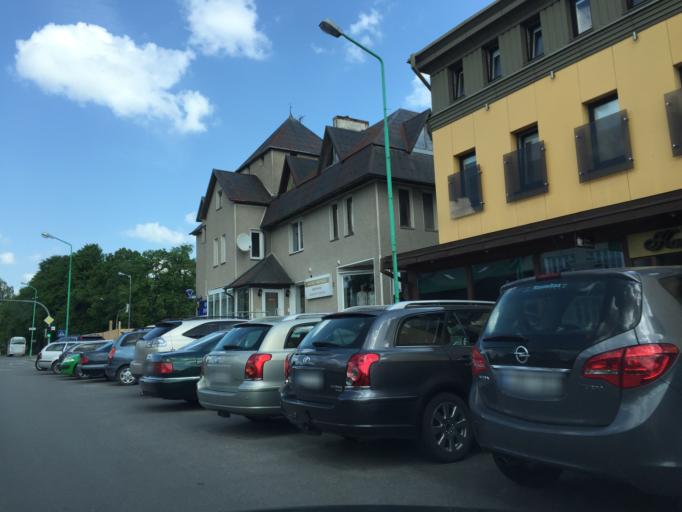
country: LT
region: Klaipedos apskritis
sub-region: Klaipeda
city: Palanga
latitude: 55.9162
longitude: 21.0704
